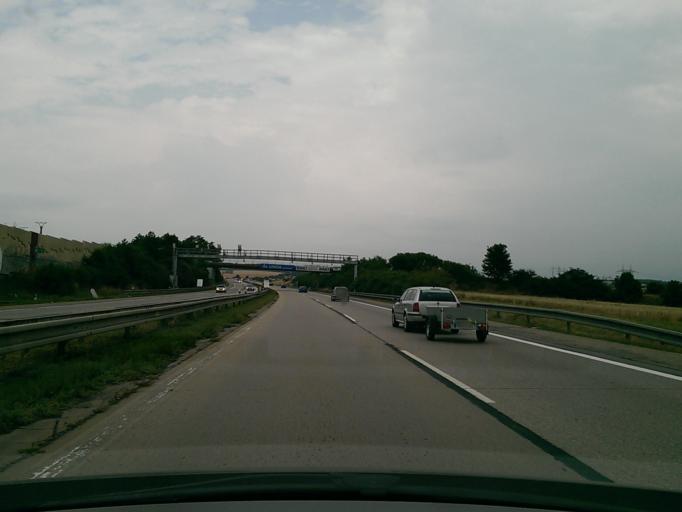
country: CZ
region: South Moravian
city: Ricany
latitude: 49.2188
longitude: 16.4055
